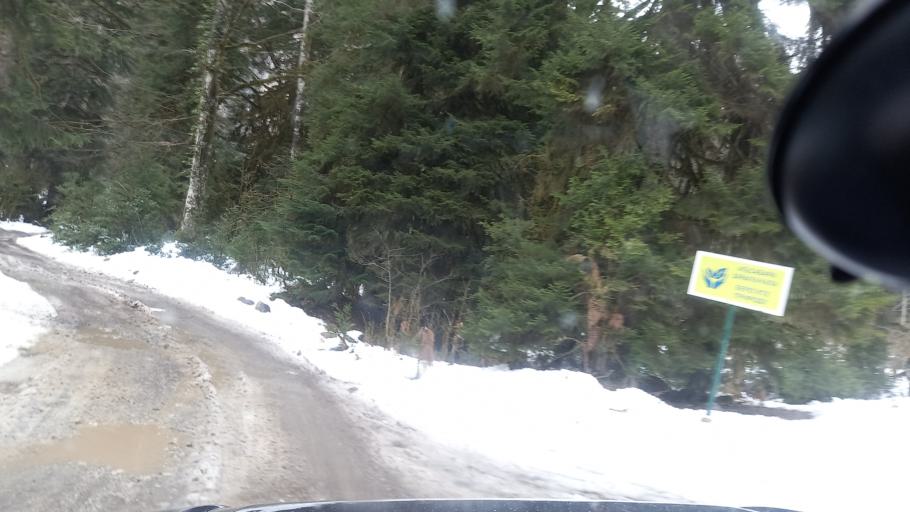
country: GE
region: Abkhazia
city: Gagra
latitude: 43.4326
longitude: 40.4460
